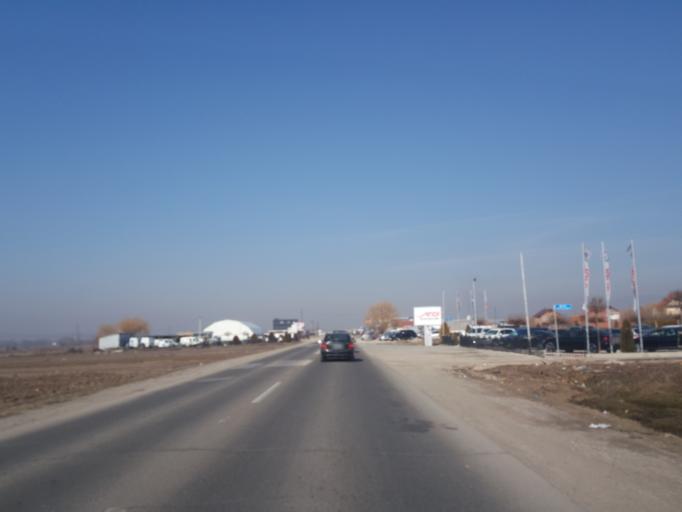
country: XK
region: Mitrovica
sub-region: Vushtrri
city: Vushtrri
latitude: 42.7648
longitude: 21.0266
